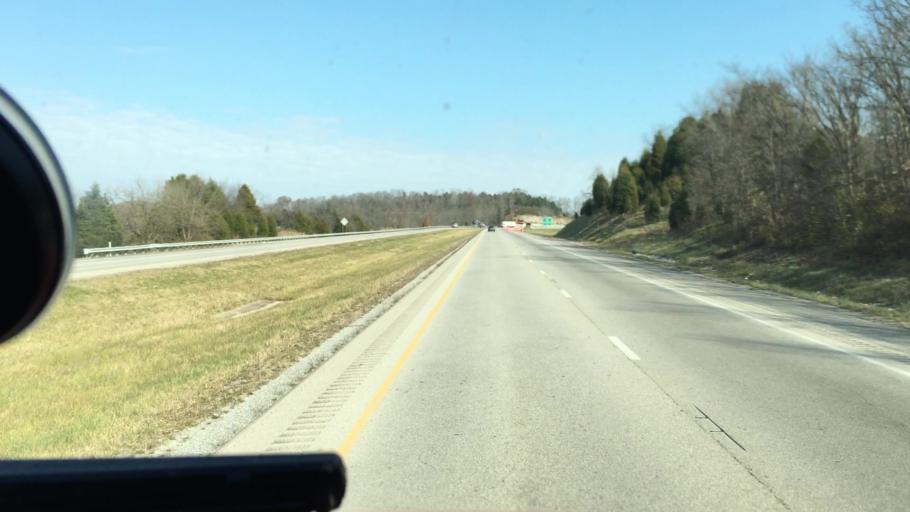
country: US
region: Kentucky
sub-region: Bath County
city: Owingsville
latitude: 38.1203
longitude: -83.7958
